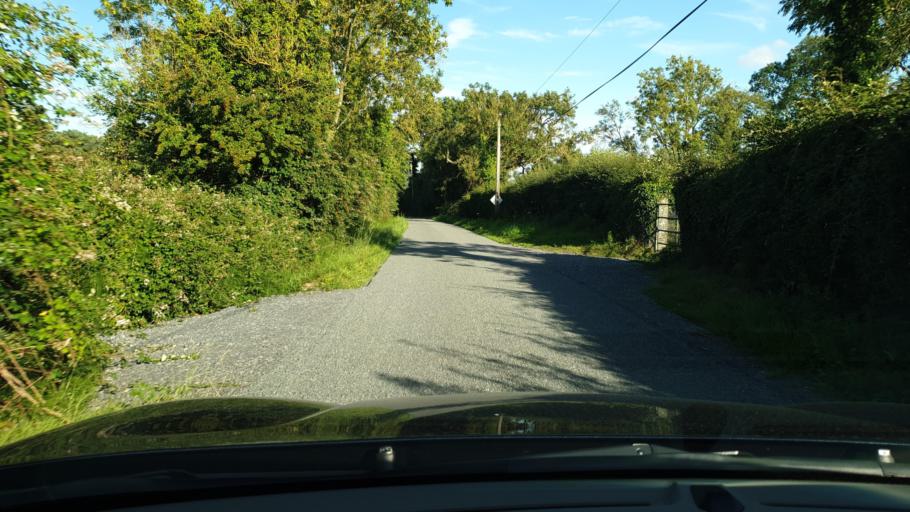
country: IE
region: Leinster
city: Balrothery
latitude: 53.5790
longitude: -6.2394
